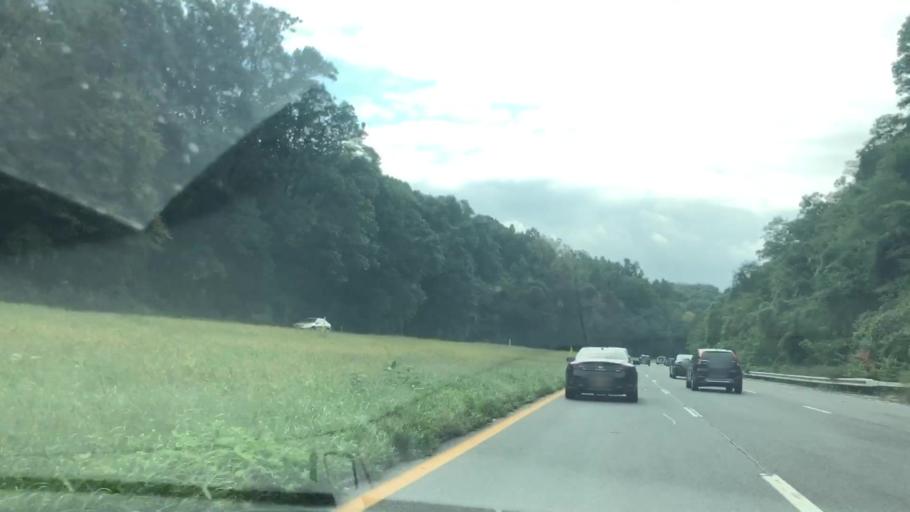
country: US
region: New York
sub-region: Westchester County
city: Yonkers
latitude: 40.9418
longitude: -73.8757
